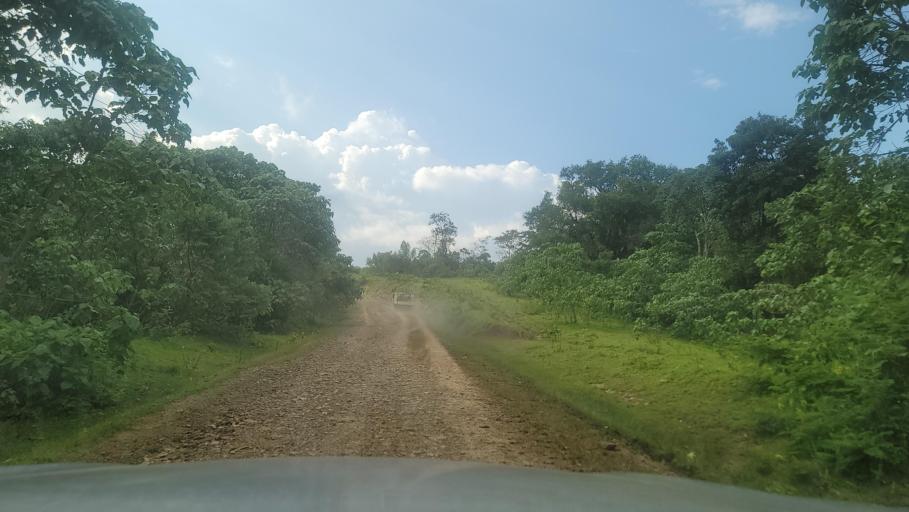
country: ET
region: Southern Nations, Nationalities, and People's Region
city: Bonga
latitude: 7.5778
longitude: 36.1604
